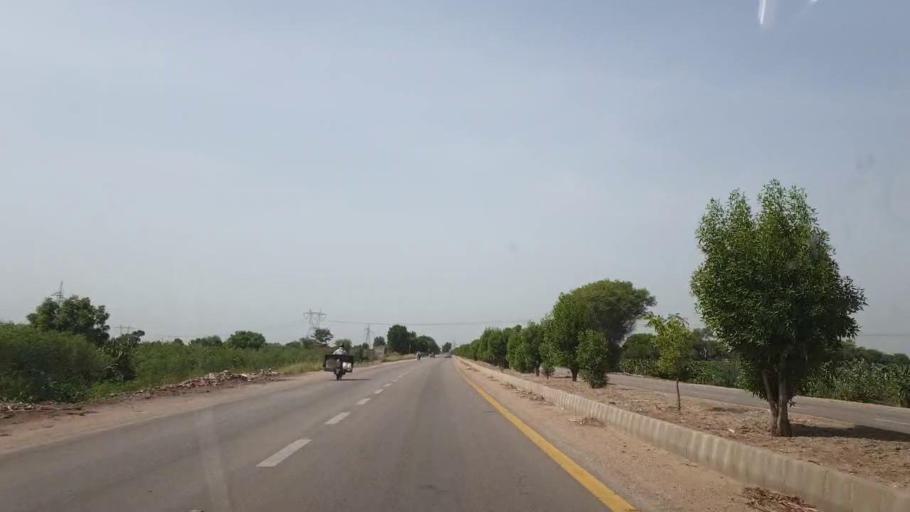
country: PK
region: Sindh
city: Sakrand
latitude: 26.1866
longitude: 68.2910
